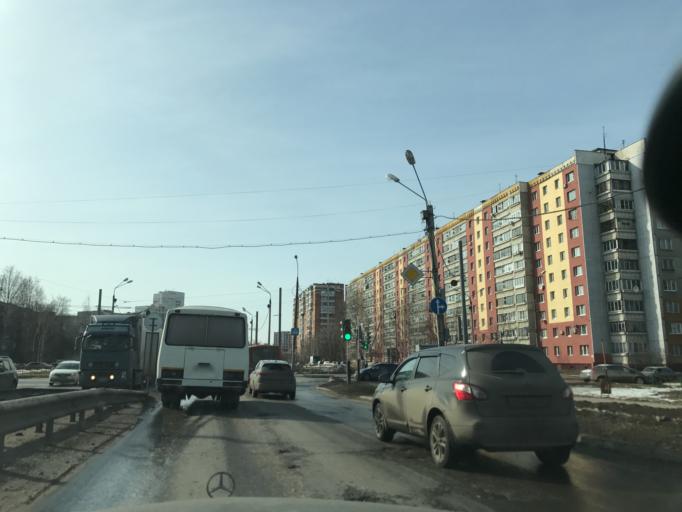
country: RU
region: Nizjnij Novgorod
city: Gorbatovka
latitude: 56.2617
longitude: 43.8641
